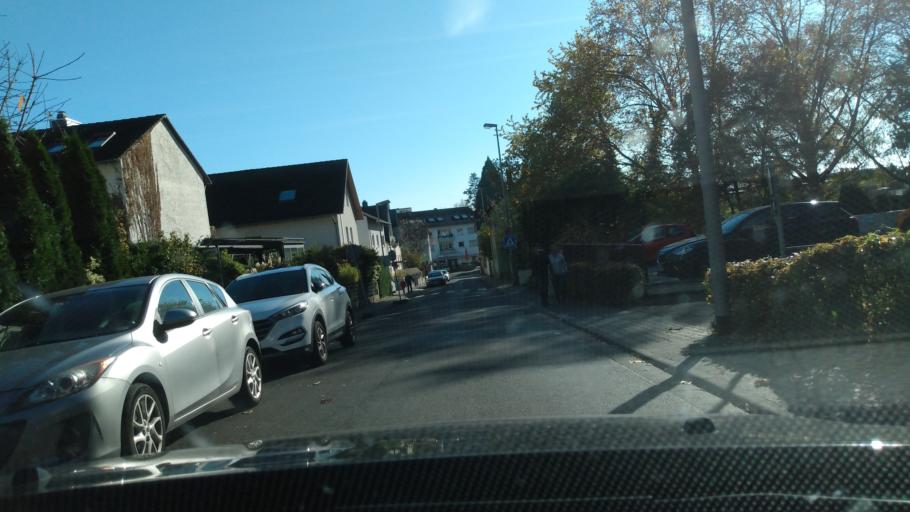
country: DE
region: Hesse
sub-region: Regierungsbezirk Darmstadt
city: Kriftel
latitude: 50.0861
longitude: 8.4700
